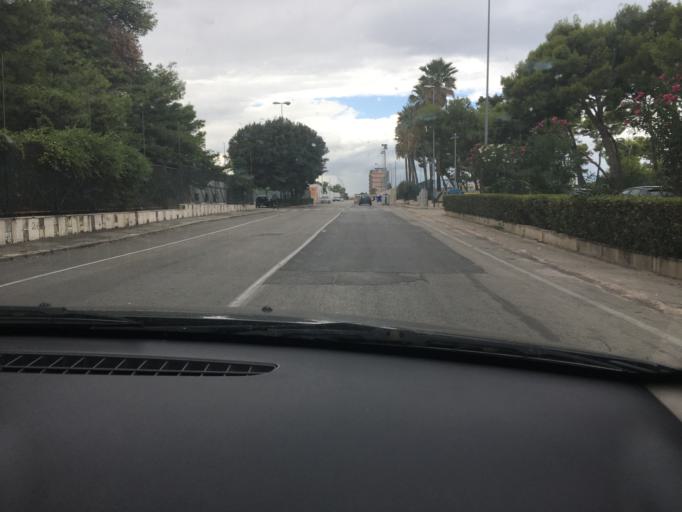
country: IT
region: Apulia
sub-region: Provincia di Bari
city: Bari
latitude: 41.1325
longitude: 16.8315
